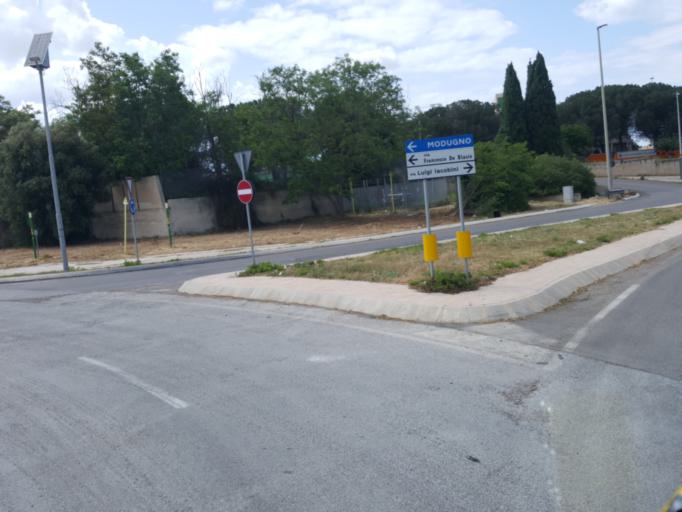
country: IT
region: Apulia
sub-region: Provincia di Bari
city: San Paolo
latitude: 41.1146
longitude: 16.8051
